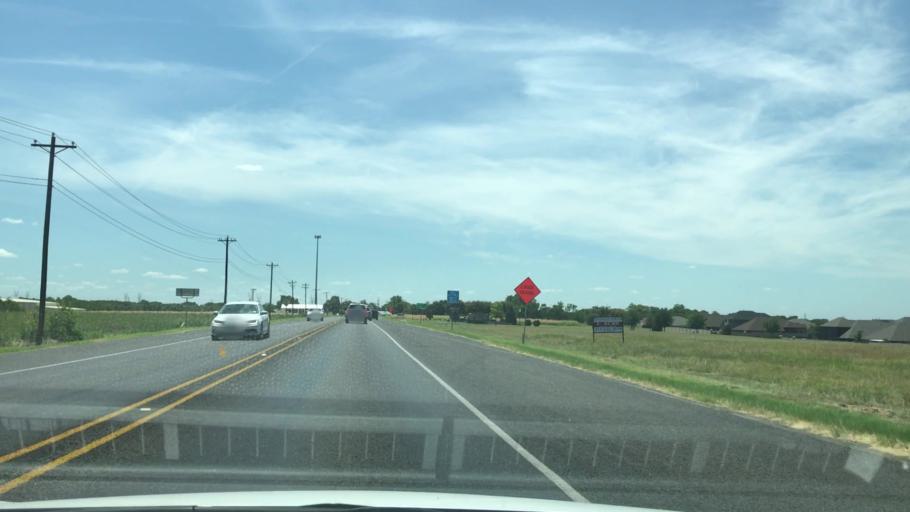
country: US
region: Texas
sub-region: Collin County
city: Lavon
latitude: 33.0207
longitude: -96.4564
